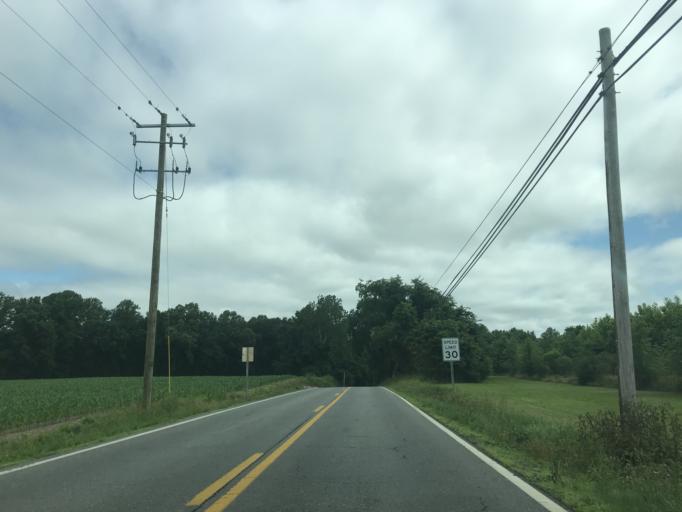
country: US
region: Maryland
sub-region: Caroline County
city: Ridgely
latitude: 38.9136
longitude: -75.9555
